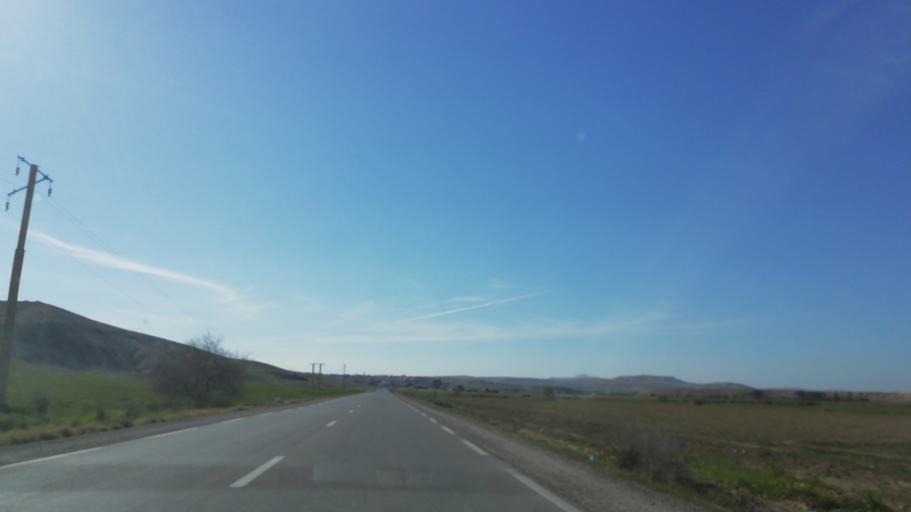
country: DZ
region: Mascara
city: Oued el Abtal
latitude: 35.4555
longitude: 0.7375
